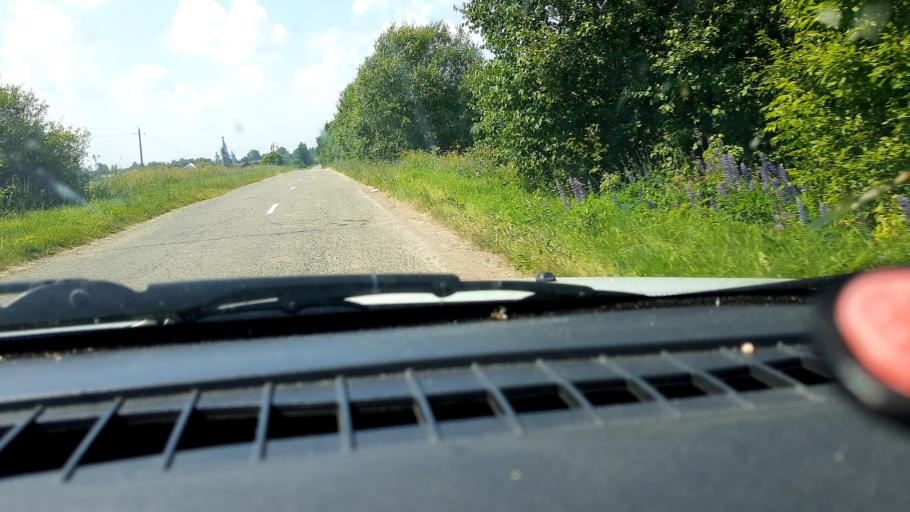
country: RU
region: Nizjnij Novgorod
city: Sharanga
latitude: 57.0541
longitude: 46.5621
